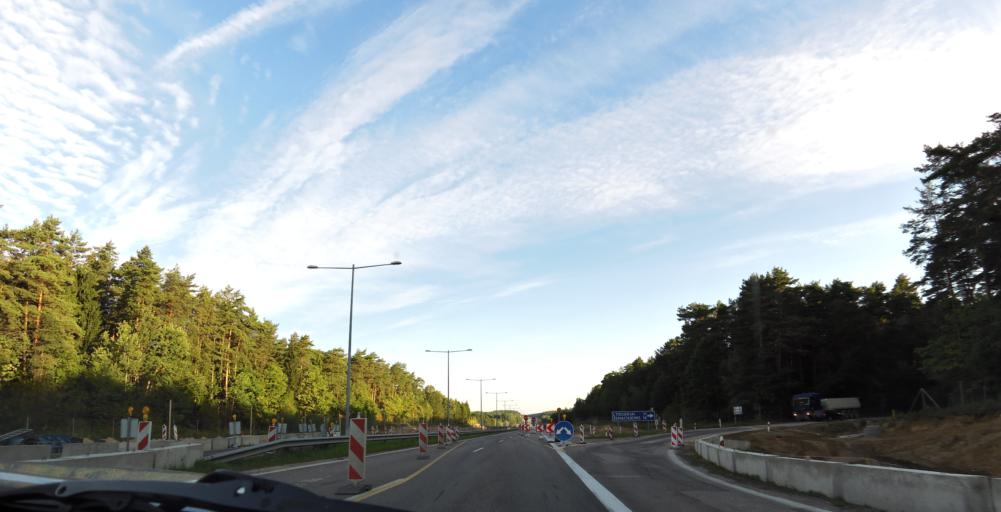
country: LT
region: Vilnius County
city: Ukmerge
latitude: 55.2475
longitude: 24.8191
